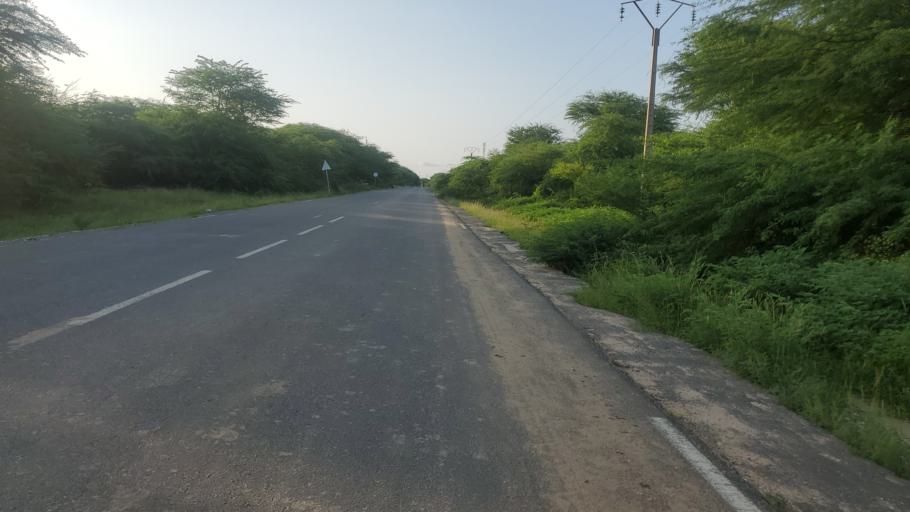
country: SN
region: Saint-Louis
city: Saint-Louis
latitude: 16.2002
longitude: -16.4115
